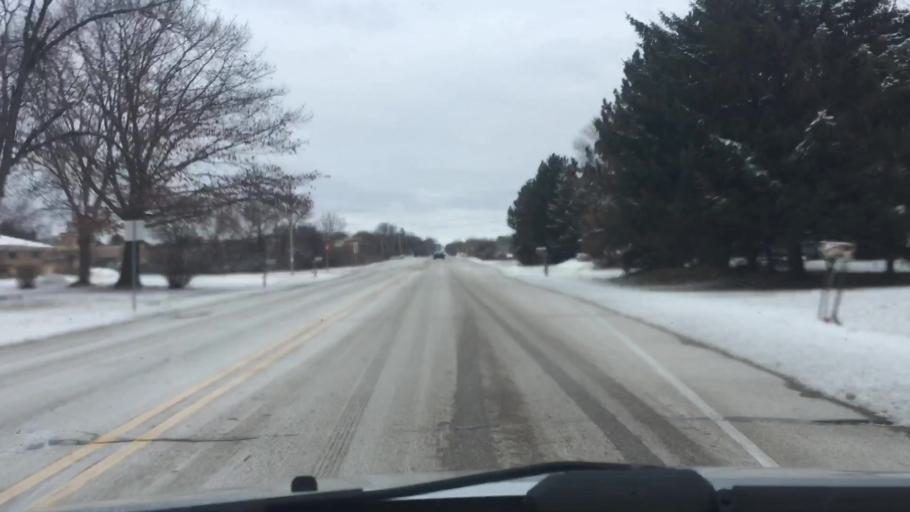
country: US
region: Wisconsin
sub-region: Waukesha County
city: Brookfield
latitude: 43.0875
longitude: -88.1059
